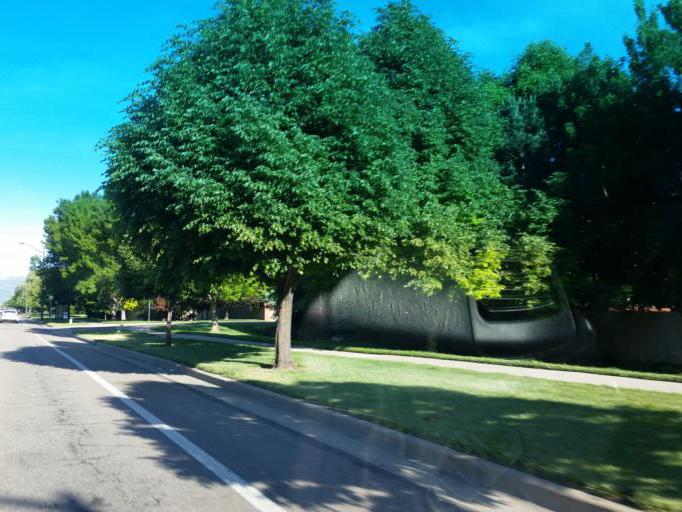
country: US
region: Colorado
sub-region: Larimer County
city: Fort Collins
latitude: 40.5380
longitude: -105.0258
